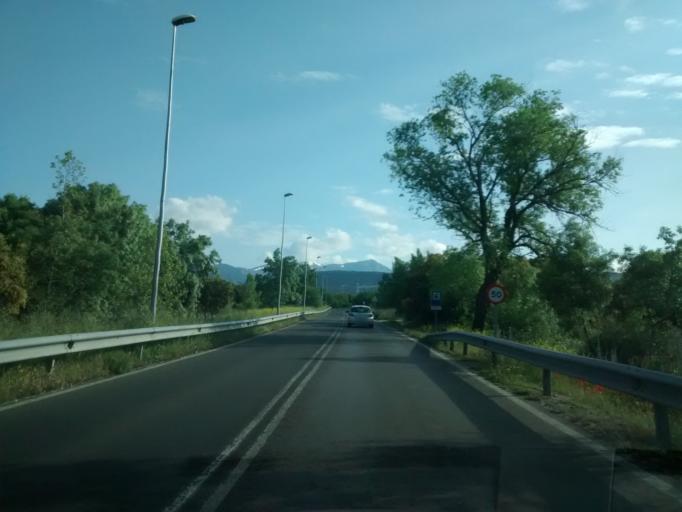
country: ES
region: Madrid
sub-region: Provincia de Madrid
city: Alpedrete
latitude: 40.6507
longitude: -4.0208
